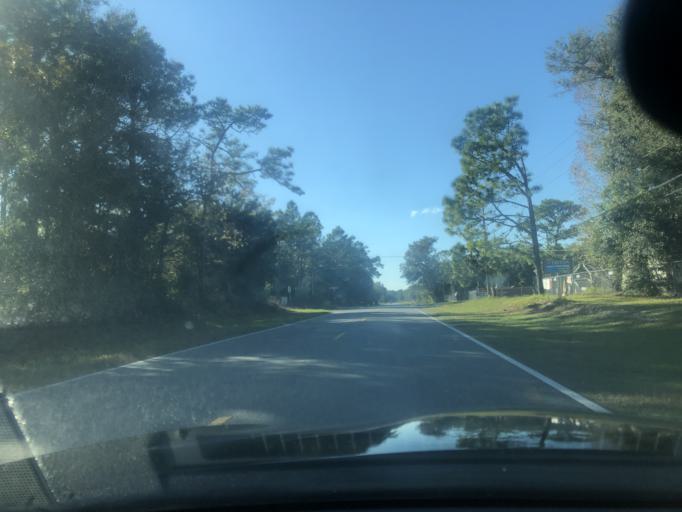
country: US
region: Florida
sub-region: Citrus County
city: Homosassa Springs
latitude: 28.8185
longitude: -82.5494
